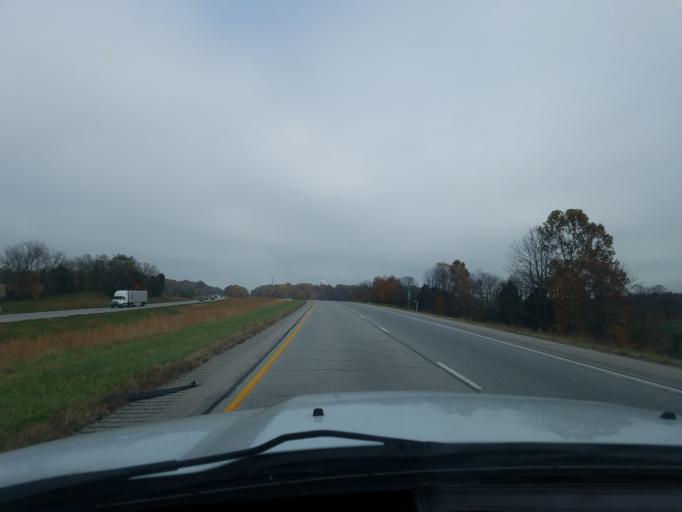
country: US
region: Indiana
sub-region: Harrison County
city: Corydon
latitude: 38.2466
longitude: -86.0721
